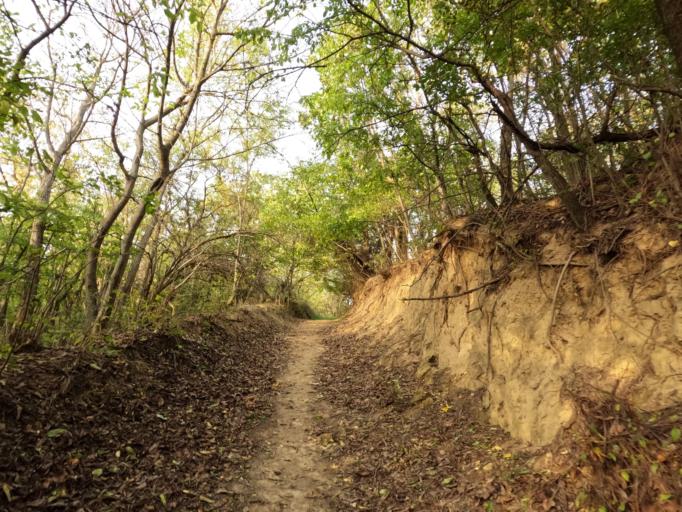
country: HU
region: Tolna
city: Szekszard
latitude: 46.3419
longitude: 18.6731
